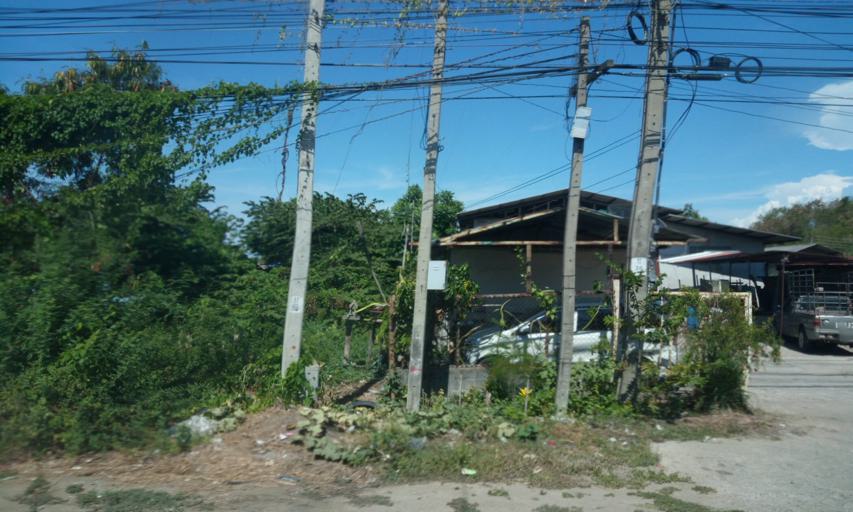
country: TH
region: Samut Prakan
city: Bang Bo District
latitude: 13.5254
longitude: 100.7884
